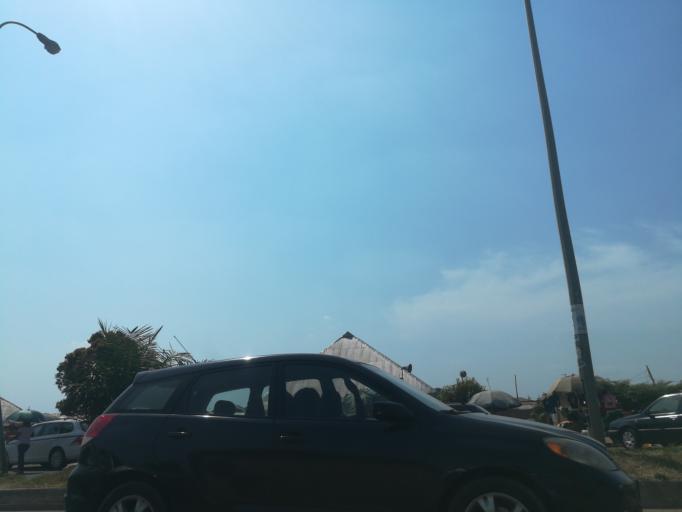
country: NG
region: Abuja Federal Capital Territory
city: Abuja
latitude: 9.0703
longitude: 7.4462
